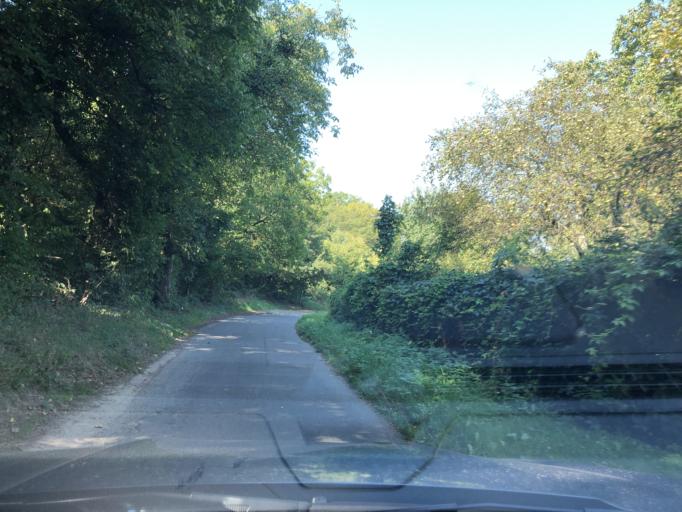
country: DE
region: Baden-Wuerttemberg
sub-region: Karlsruhe Region
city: Leimen
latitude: 49.3644
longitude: 8.6975
